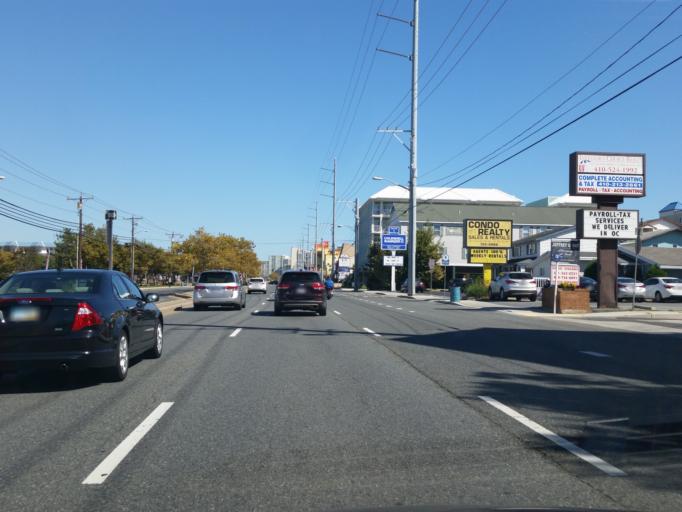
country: US
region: Maryland
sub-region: Worcester County
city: Ocean City
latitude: 38.3976
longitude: -75.0622
